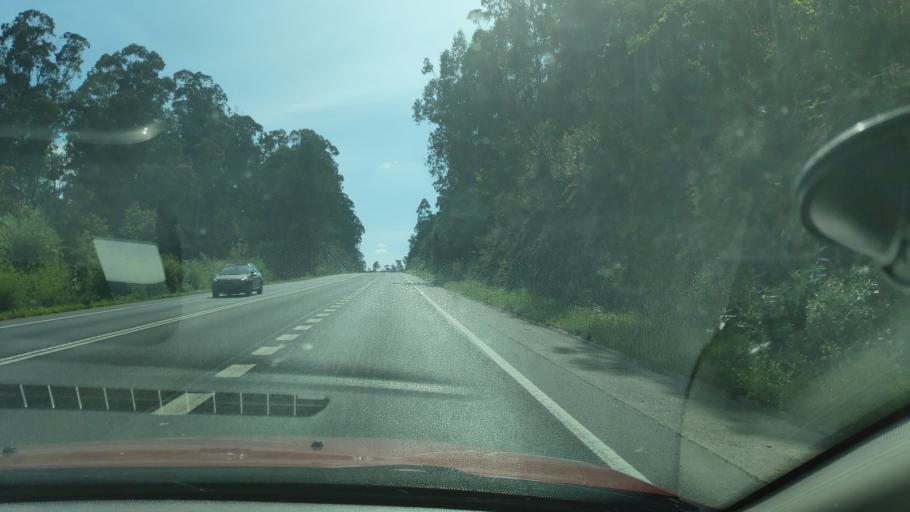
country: ES
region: Galicia
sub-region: Provincia da Coruna
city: Ames
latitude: 42.8789
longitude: -8.6677
